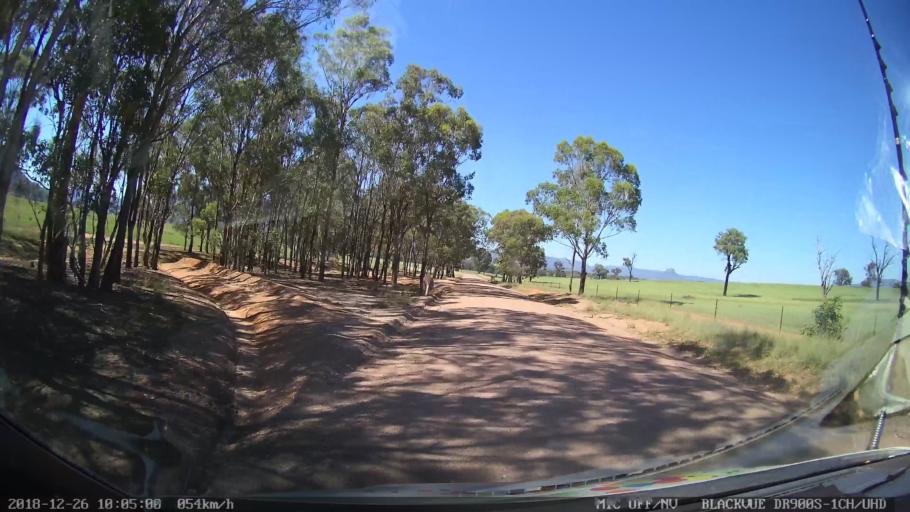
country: AU
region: New South Wales
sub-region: Mid-Western Regional
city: Kandos
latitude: -33.0748
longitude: 150.2124
